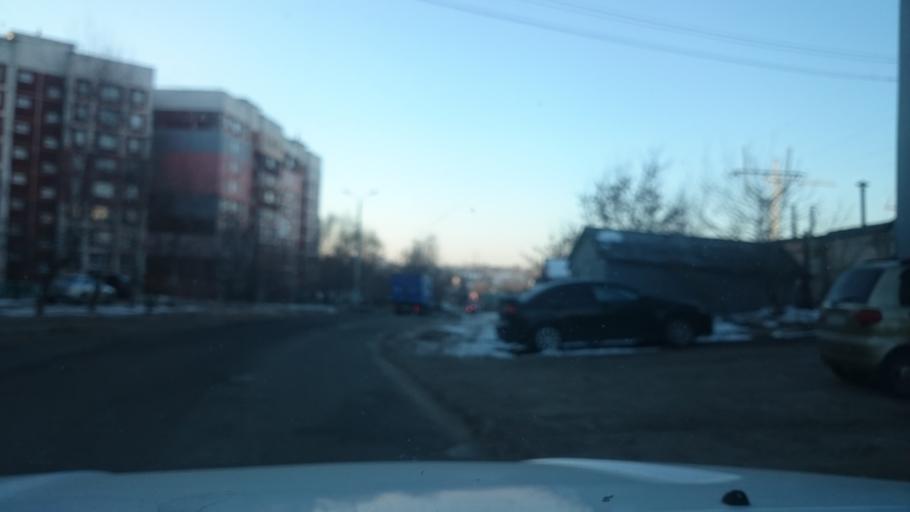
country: RU
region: Tula
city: Tula
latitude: 54.2139
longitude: 37.6886
